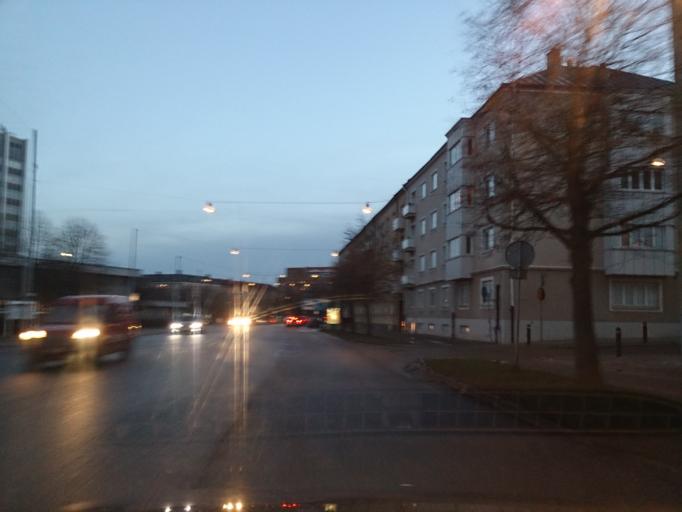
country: SE
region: OEstergoetland
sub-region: Norrkopings Kommun
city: Norrkoping
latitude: 58.5960
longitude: 16.1730
